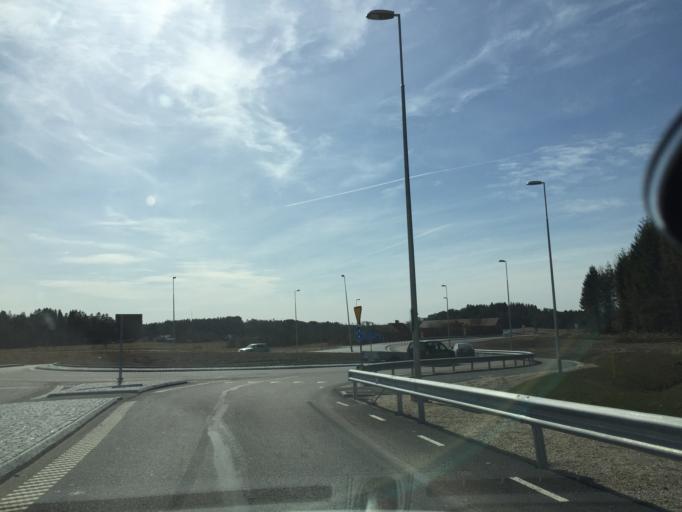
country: SE
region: Vaestra Goetaland
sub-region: Uddevalla Kommun
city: Uddevalla
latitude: 58.3508
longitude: 11.8012
